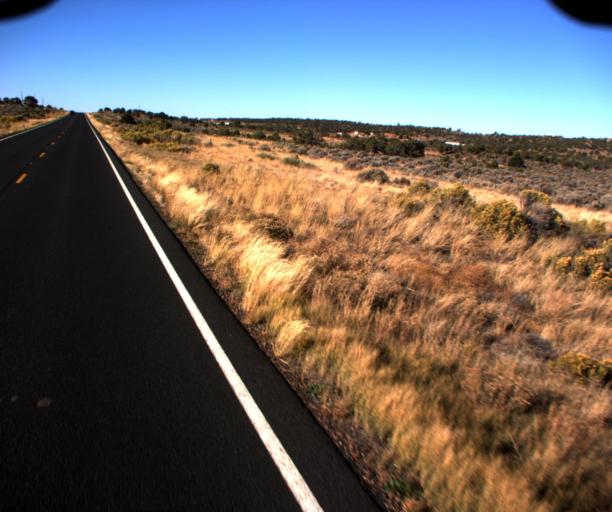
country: US
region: Arizona
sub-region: Apache County
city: Ganado
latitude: 35.7696
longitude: -109.7424
